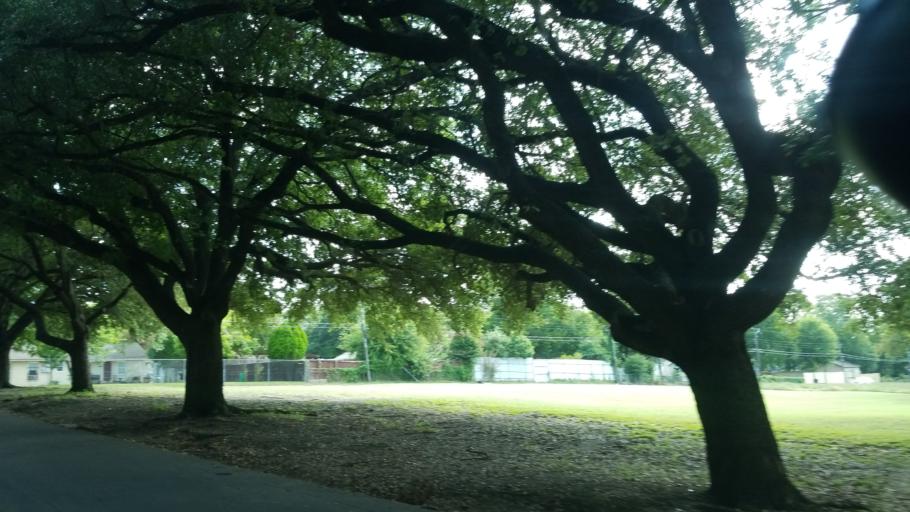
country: US
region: Texas
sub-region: Dallas County
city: Dallas
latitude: 32.7748
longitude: -96.7146
